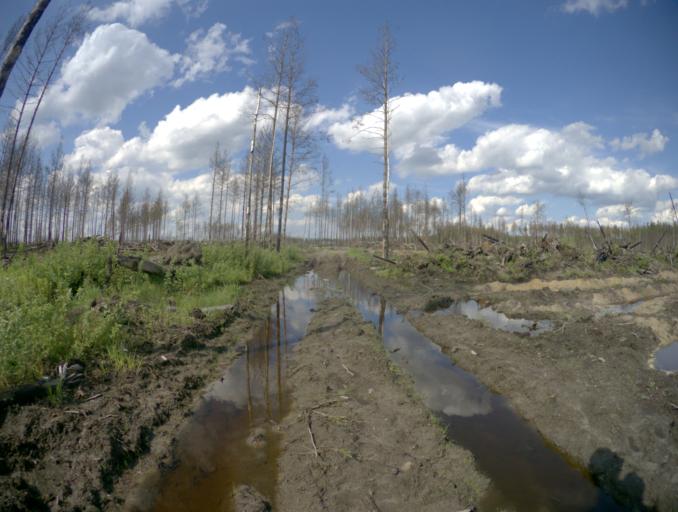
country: RU
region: Vladimir
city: Velikodvorskiy
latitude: 55.3129
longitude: 40.9185
